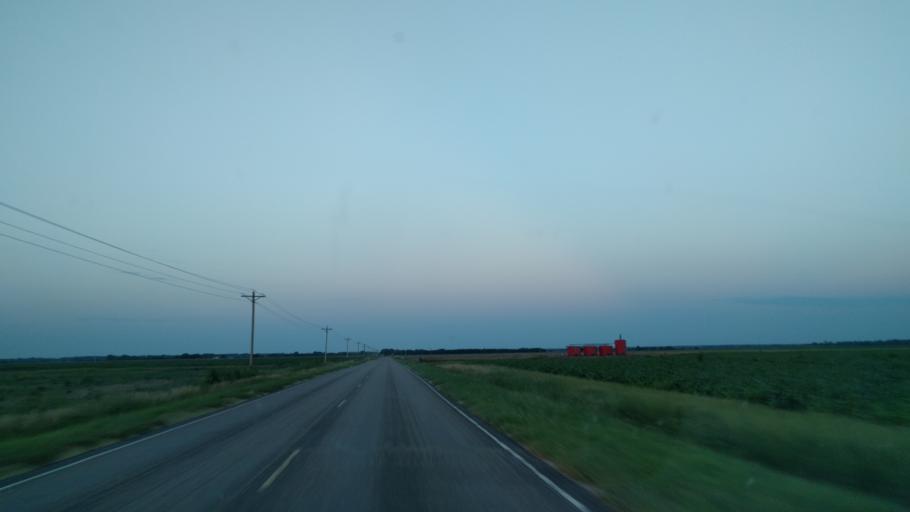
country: US
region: Kansas
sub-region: Reno County
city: Nickerson
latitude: 38.2175
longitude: -98.0997
